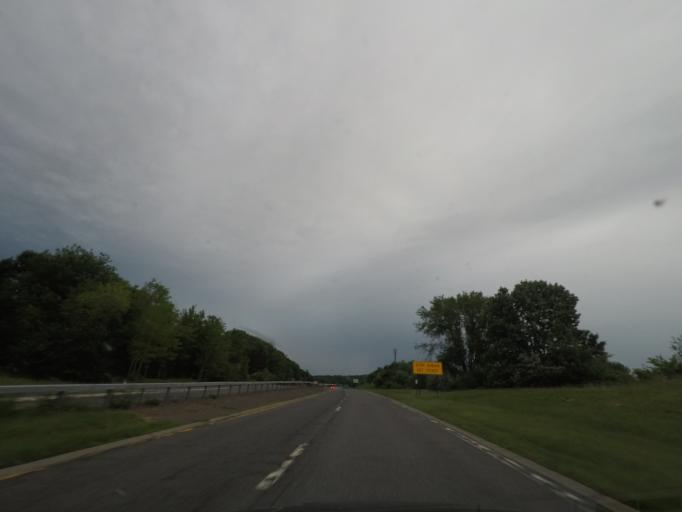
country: US
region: New York
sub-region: Columbia County
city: Chatham
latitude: 42.4145
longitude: -73.5487
